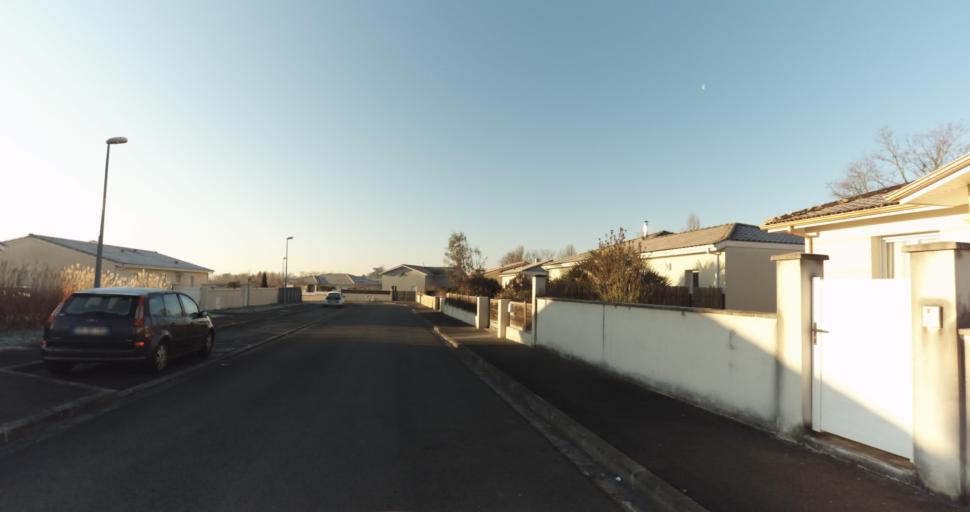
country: FR
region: Aquitaine
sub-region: Departement de la Gironde
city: Ambares-et-Lagrave
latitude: 44.9153
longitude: -0.4981
